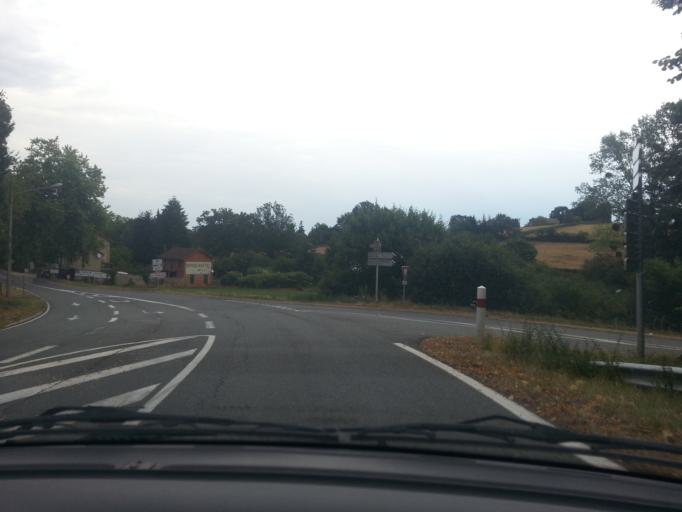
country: FR
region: Auvergne
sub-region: Departement de l'Allier
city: Le Donjon
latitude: 46.3455
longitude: 3.7930
